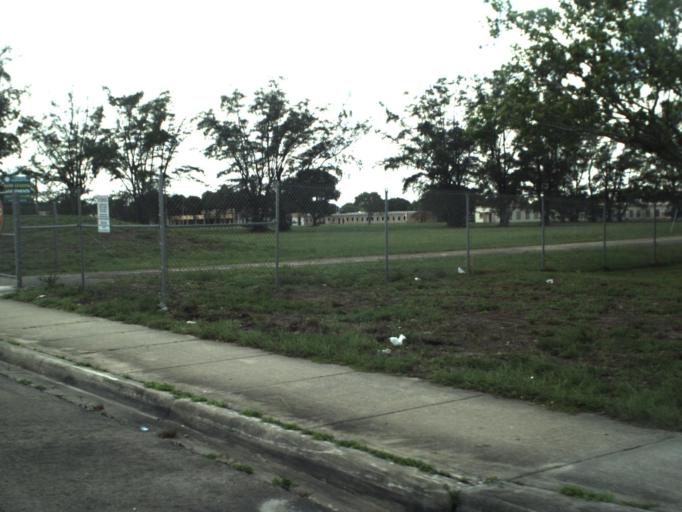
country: US
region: Florida
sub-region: Broward County
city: Miramar
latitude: 25.9948
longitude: -80.2492
